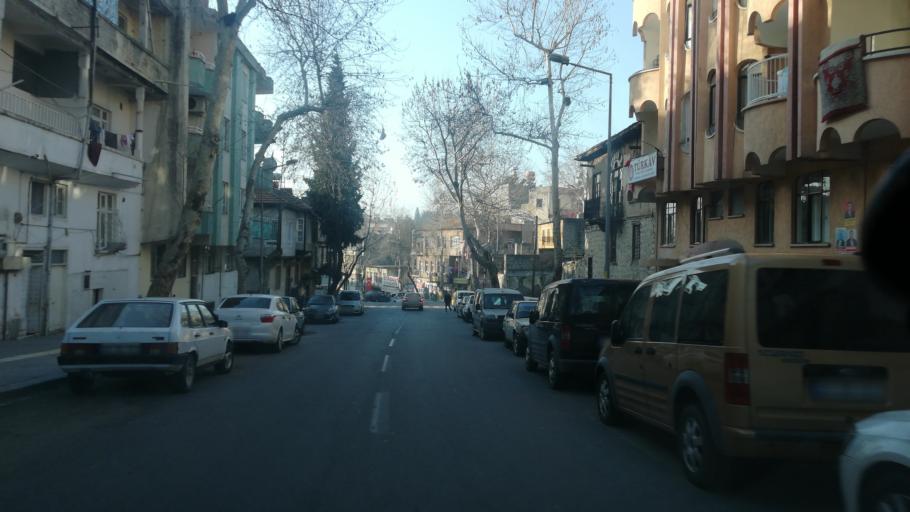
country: TR
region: Kahramanmaras
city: Kahramanmaras
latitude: 37.5906
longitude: 36.9271
